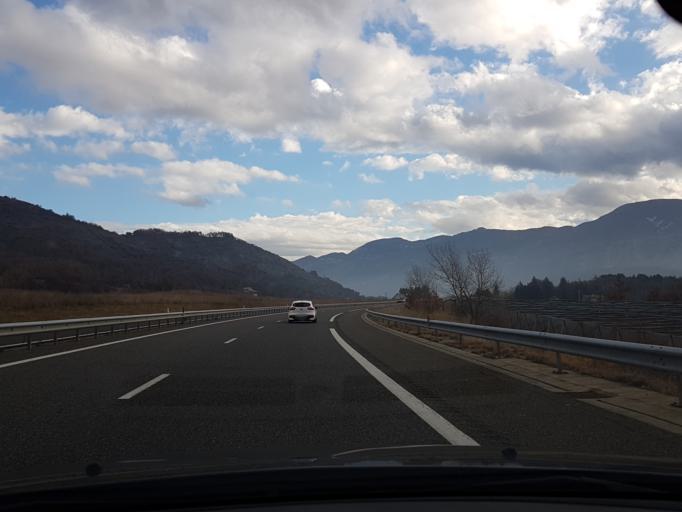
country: FR
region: Provence-Alpes-Cote d'Azur
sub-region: Departement des Hautes-Alpes
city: Tallard
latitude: 44.4179
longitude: 5.9722
